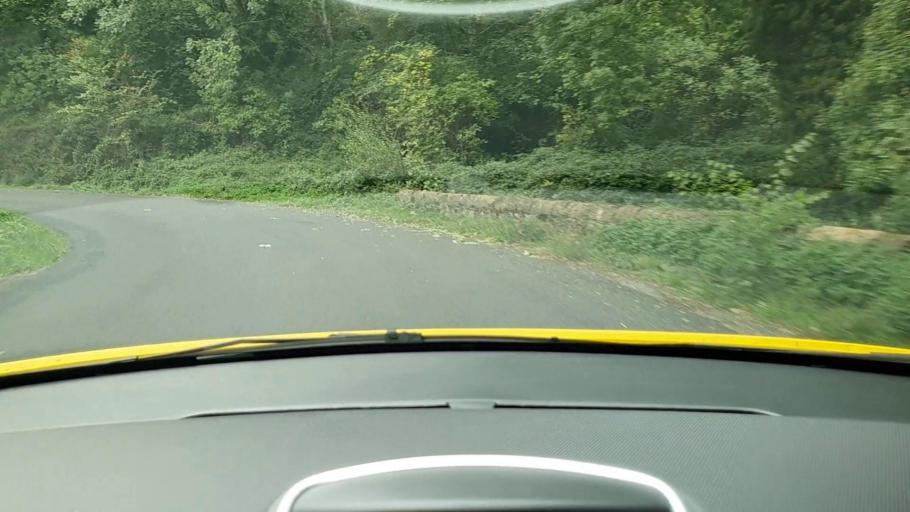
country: FR
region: Languedoc-Roussillon
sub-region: Departement de la Lozere
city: Meyrueis
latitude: 44.0692
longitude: 3.4403
